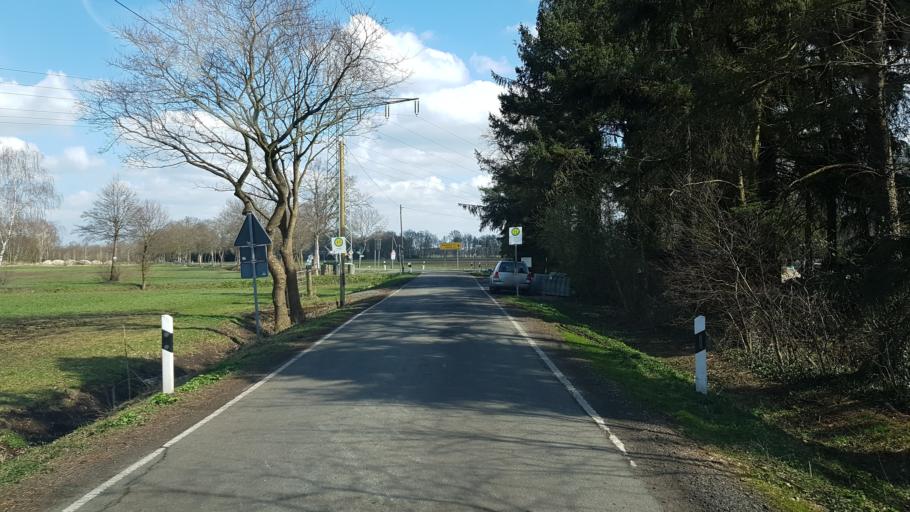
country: DE
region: Lower Saxony
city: Rastede
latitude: 53.2981
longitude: 8.2134
